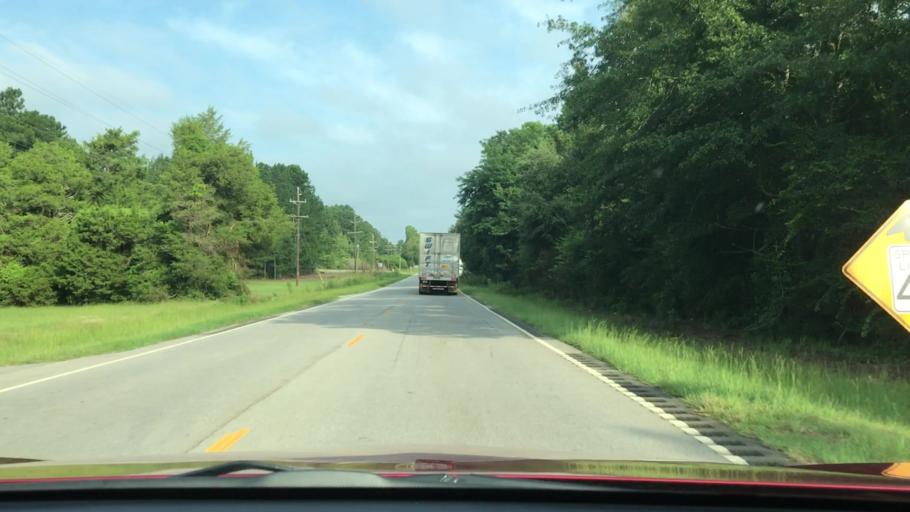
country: US
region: South Carolina
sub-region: Barnwell County
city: Williston
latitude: 33.6459
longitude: -81.3486
